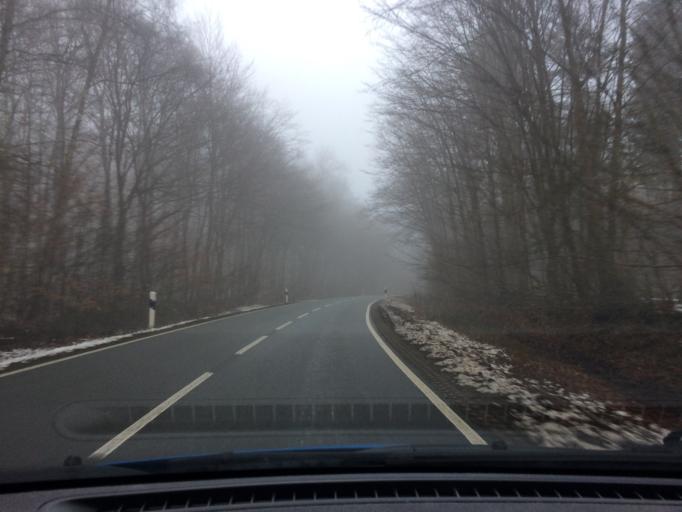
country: DE
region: Schleswig-Holstein
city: Kollow
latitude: 53.4865
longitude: 10.4670
